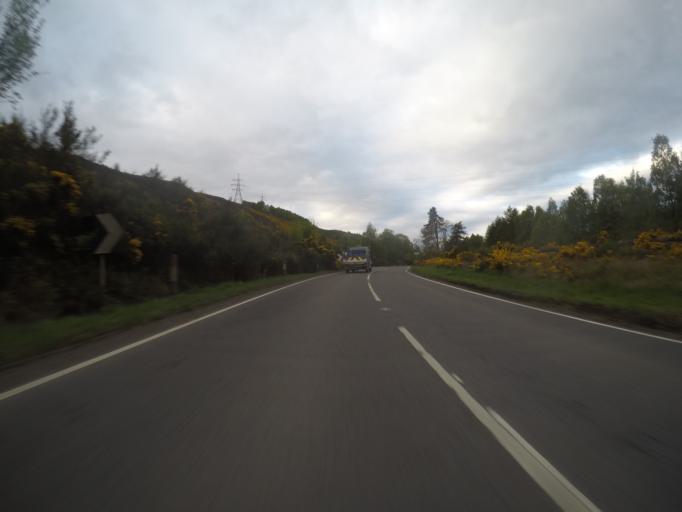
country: GB
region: Scotland
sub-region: Highland
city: Spean Bridge
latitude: 57.1250
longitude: -4.6930
